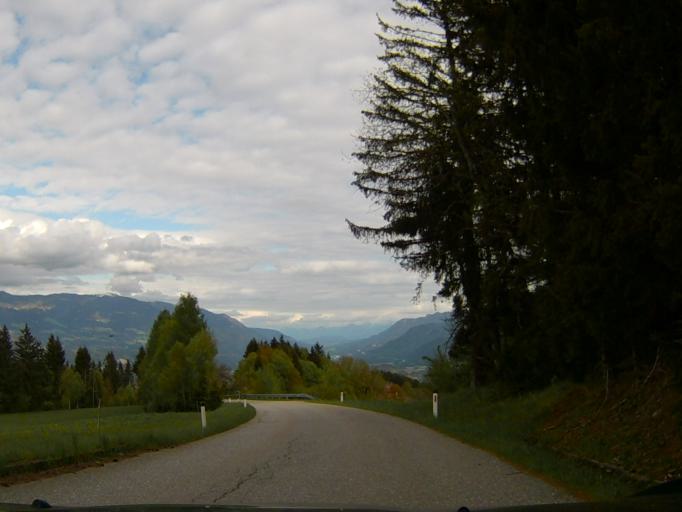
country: AT
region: Carinthia
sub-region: Politischer Bezirk Villach Land
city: Stockenboi
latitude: 46.7359
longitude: 13.5594
